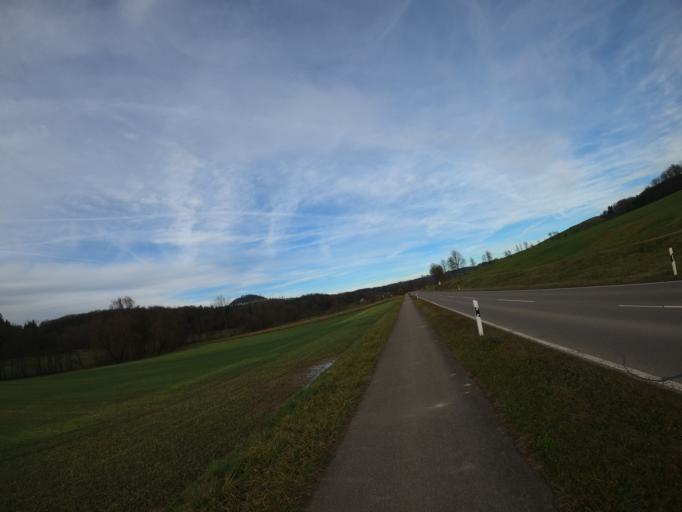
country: DE
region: Baden-Wuerttemberg
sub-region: Regierungsbezirk Stuttgart
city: Salach
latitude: 48.7152
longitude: 9.7354
